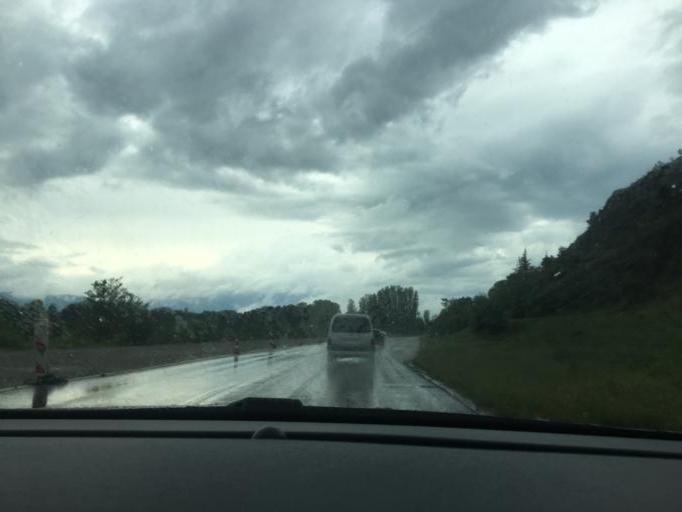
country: MK
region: Ohrid
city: Ohrid
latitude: 41.1405
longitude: 20.7628
